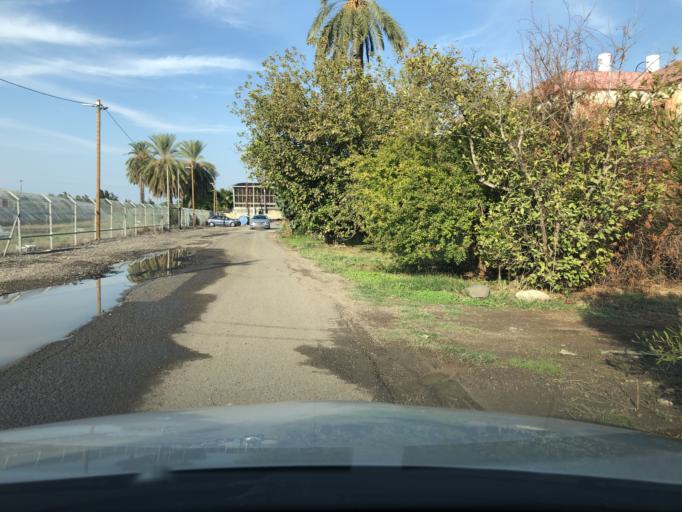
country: IL
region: Northern District
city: Yavne'el
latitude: 32.6615
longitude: 35.5795
